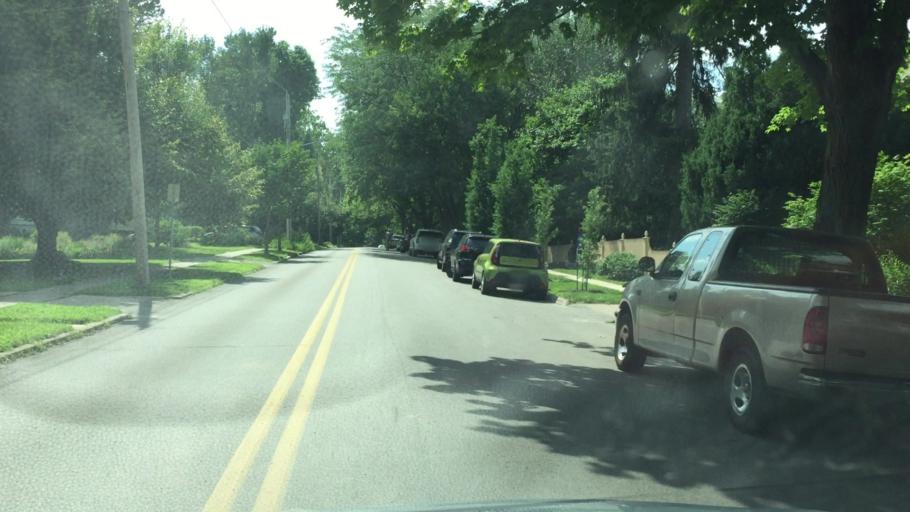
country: US
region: Iowa
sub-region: Johnson County
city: Iowa City
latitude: 41.6567
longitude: -91.5177
